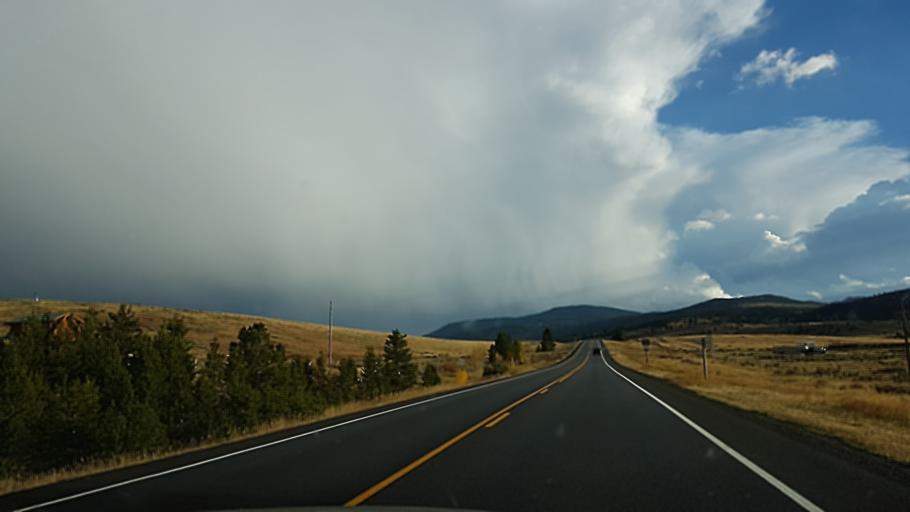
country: US
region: Montana
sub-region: Gallatin County
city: West Yellowstone
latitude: 44.7258
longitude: -111.4708
